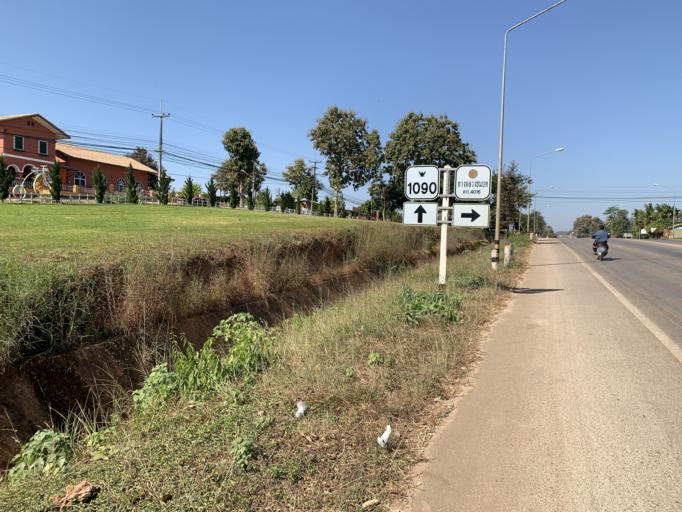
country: TH
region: Tak
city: Phop Phra
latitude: 16.5323
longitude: 98.7025
